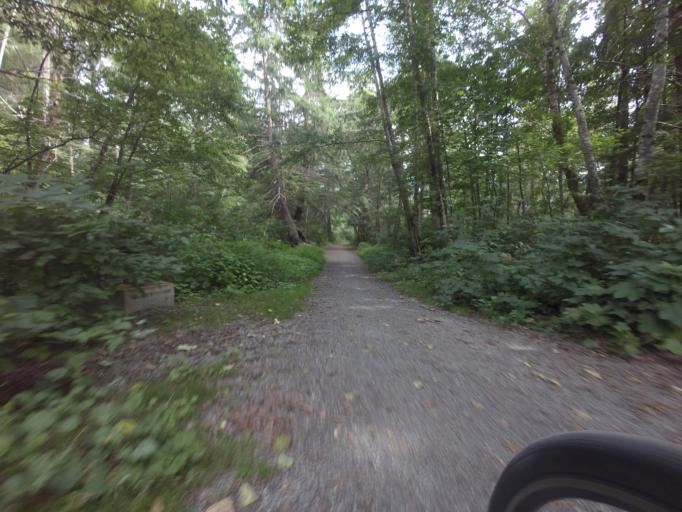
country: CA
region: British Columbia
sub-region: Greater Vancouver Regional District
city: Lions Bay
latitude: 49.7097
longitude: -123.1518
